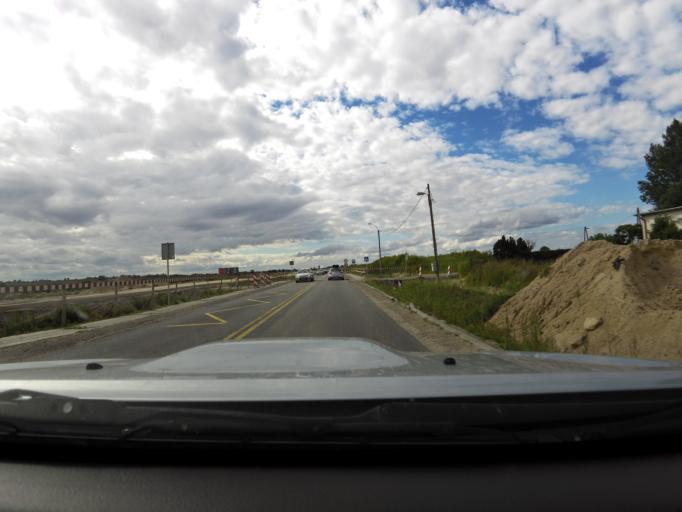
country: PL
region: Pomeranian Voivodeship
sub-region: Powiat nowodworski
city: Ostaszewo
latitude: 54.2387
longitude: 19.0247
